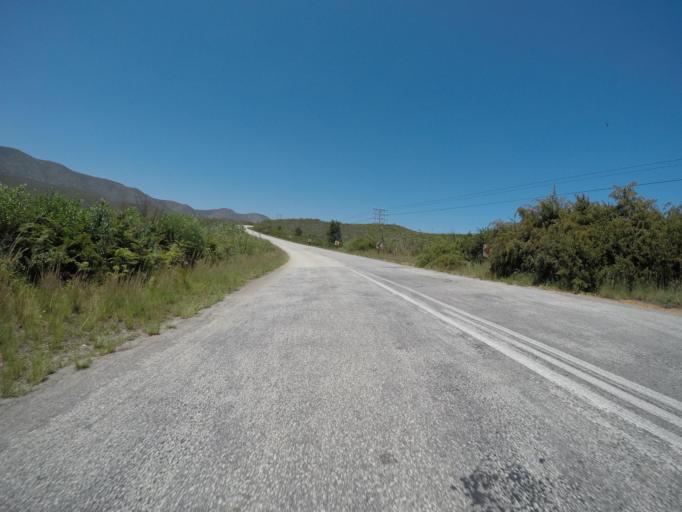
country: ZA
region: Eastern Cape
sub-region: Cacadu District Municipality
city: Kareedouw
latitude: -33.8864
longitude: 24.0784
